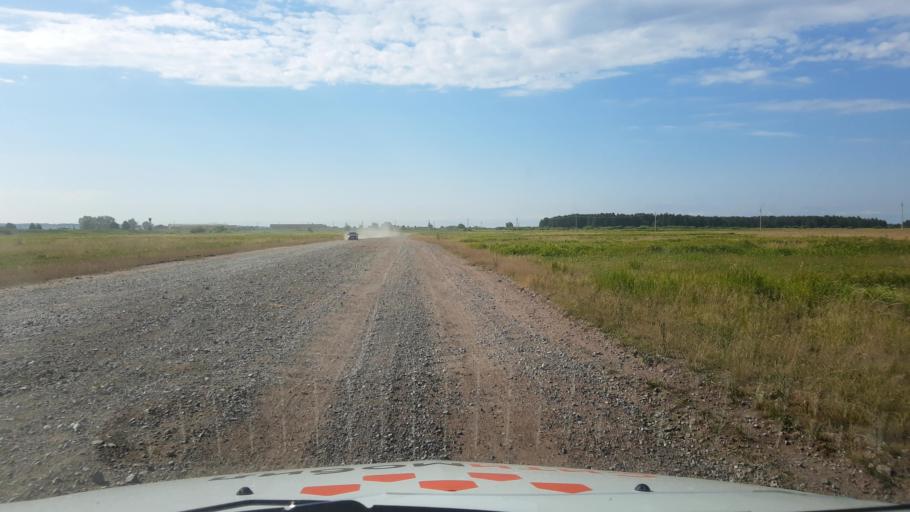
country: RU
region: Bashkortostan
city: Mikhaylovka
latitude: 54.9682
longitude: 55.7981
